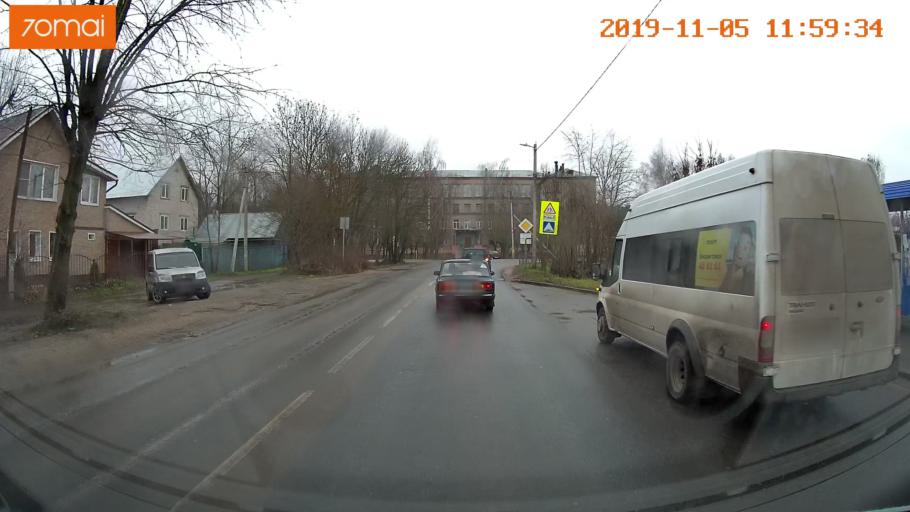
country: RU
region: Ivanovo
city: Kokhma
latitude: 56.9779
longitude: 41.0492
